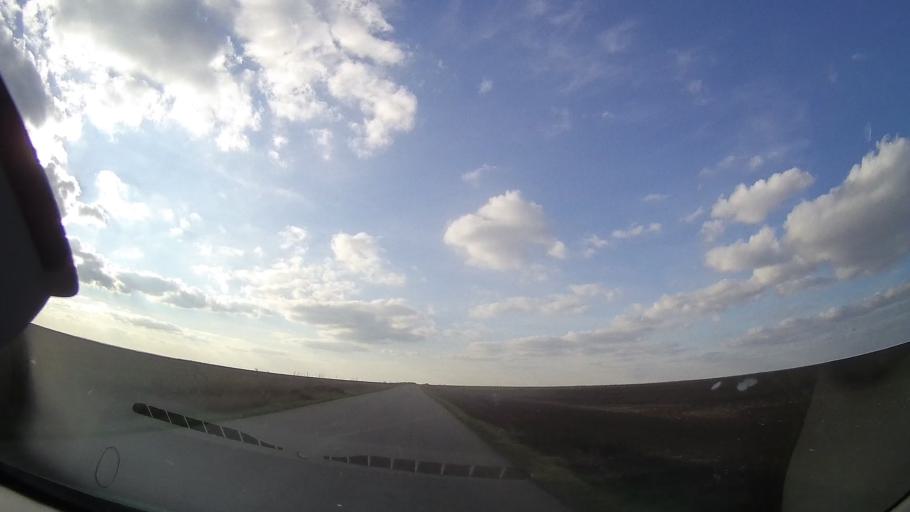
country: RO
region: Constanta
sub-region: Comuna Cerchezu
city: Cerchezu
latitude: 43.8234
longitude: 28.1473
